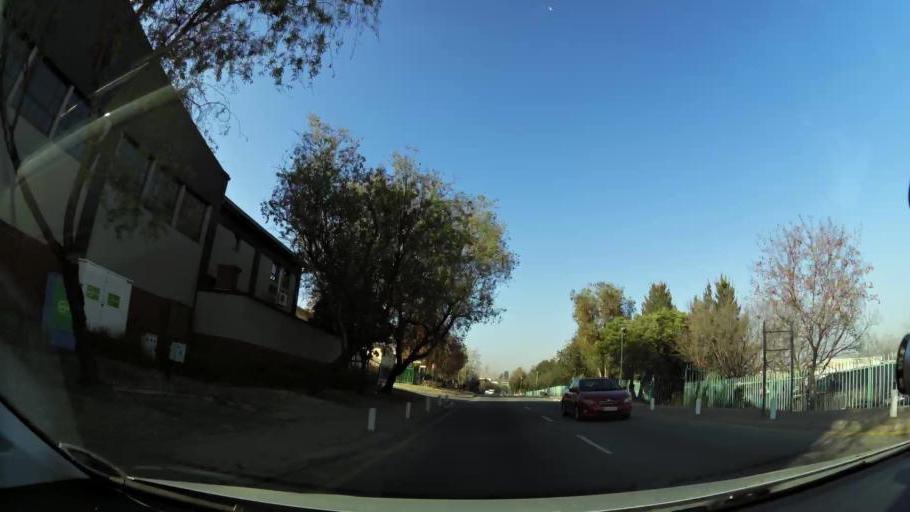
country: ZA
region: Gauteng
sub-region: City of Johannesburg Metropolitan Municipality
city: Modderfontein
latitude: -26.0771
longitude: 28.1167
